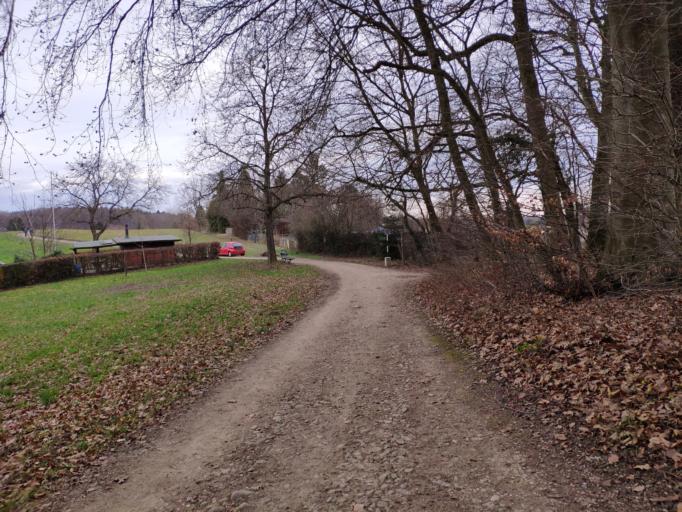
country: CH
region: Basel-City
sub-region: Basel-Stadt
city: Bettingen
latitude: 47.5652
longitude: 7.6652
